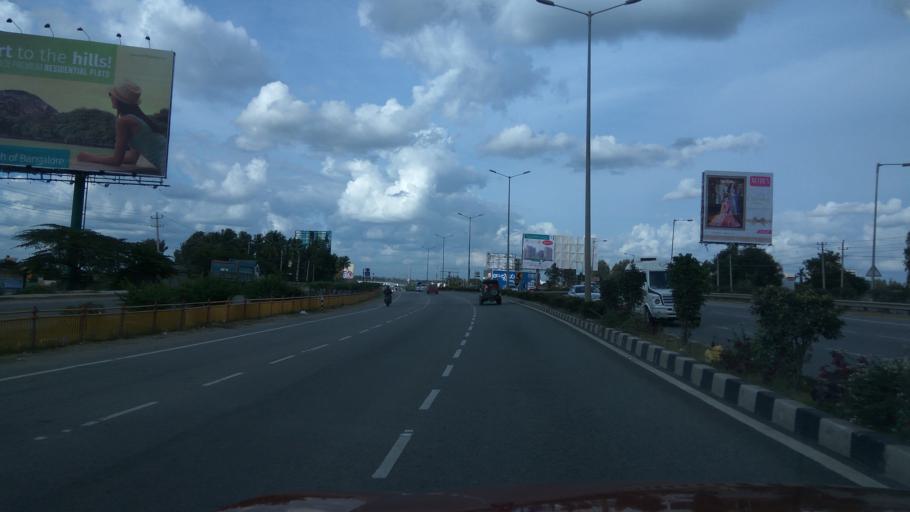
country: IN
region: Karnataka
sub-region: Bangalore Urban
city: Yelahanka
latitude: 13.1647
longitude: 77.6295
